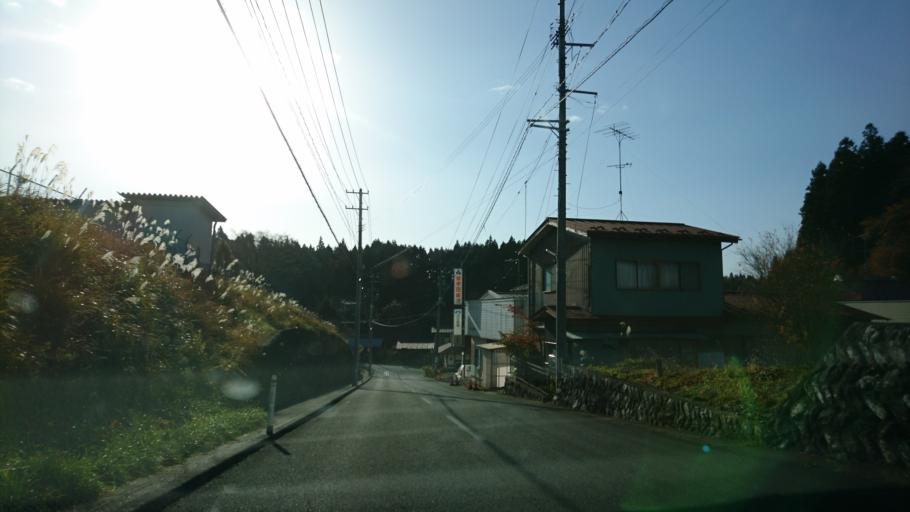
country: JP
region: Iwate
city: Ichinoseki
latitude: 38.8604
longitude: 141.3418
